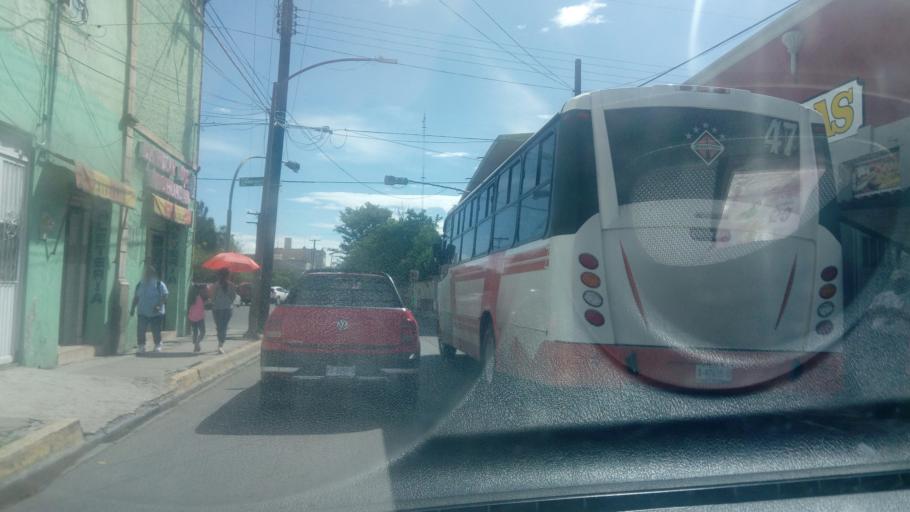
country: MX
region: Durango
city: Victoria de Durango
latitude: 24.0235
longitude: -104.6619
